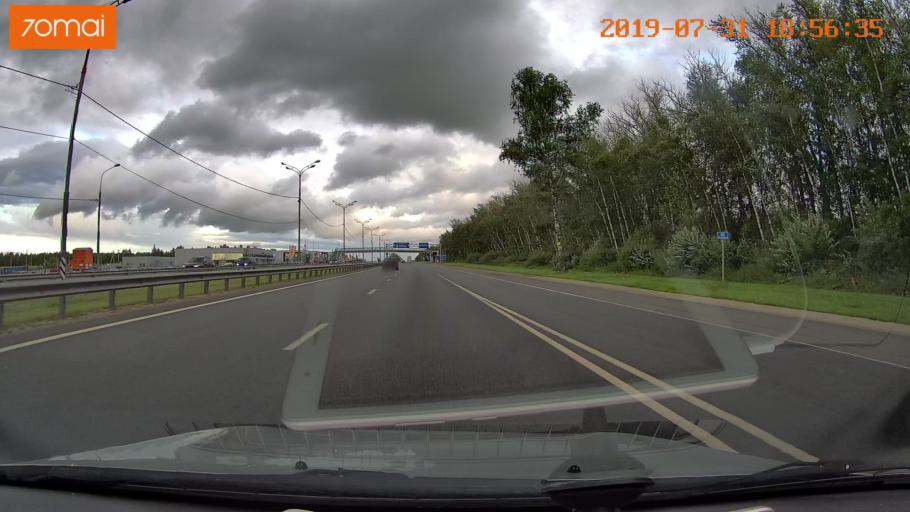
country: RU
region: Moskovskaya
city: Raduzhnyy
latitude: 55.1616
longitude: 38.6801
